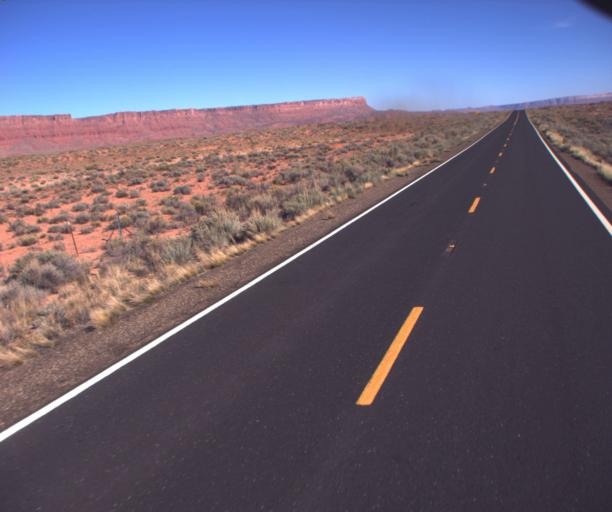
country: US
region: Arizona
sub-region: Coconino County
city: Page
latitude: 36.7149
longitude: -111.9902
